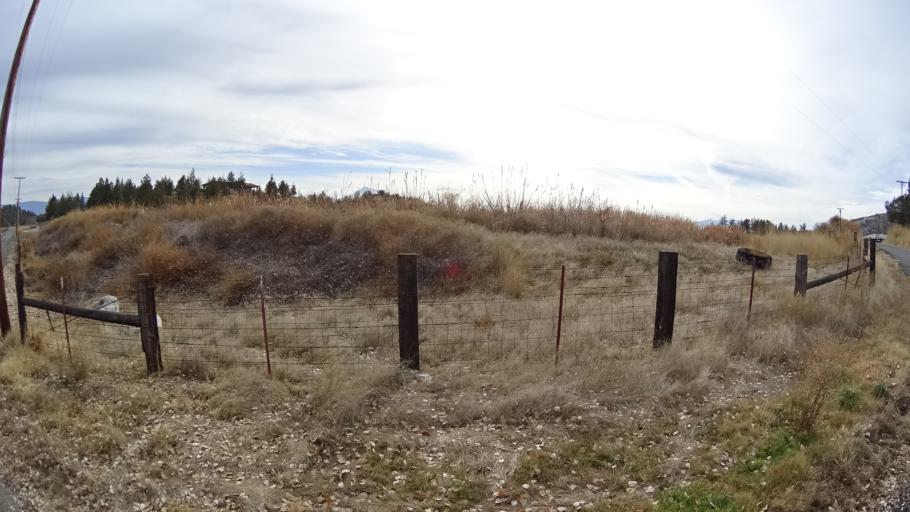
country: US
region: California
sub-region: Siskiyou County
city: Montague
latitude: 41.6832
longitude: -122.5245
